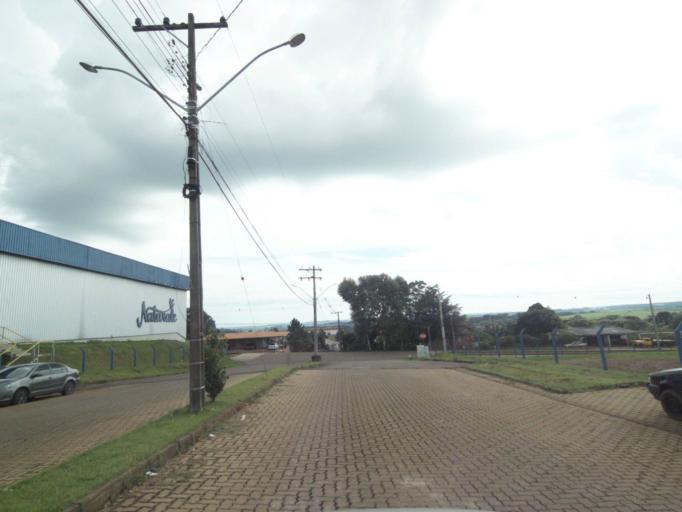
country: BR
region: Rio Grande do Sul
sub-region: Lagoa Vermelha
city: Lagoa Vermelha
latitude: -28.2243
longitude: -51.5104
